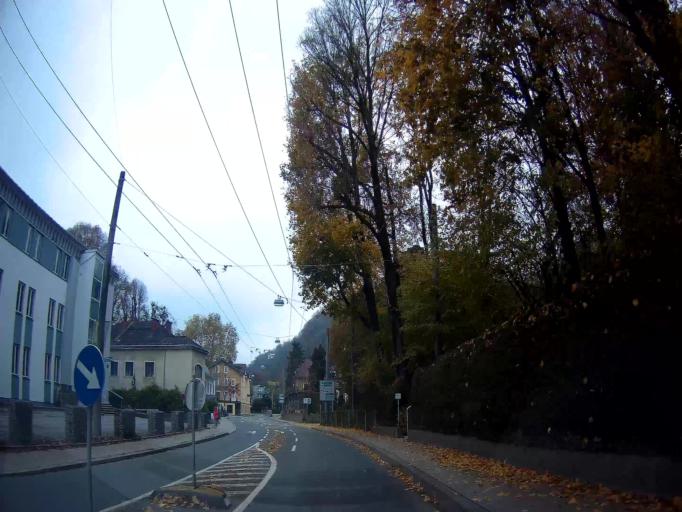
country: AT
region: Salzburg
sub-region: Salzburg Stadt
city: Salzburg
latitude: 47.7985
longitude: 13.0655
